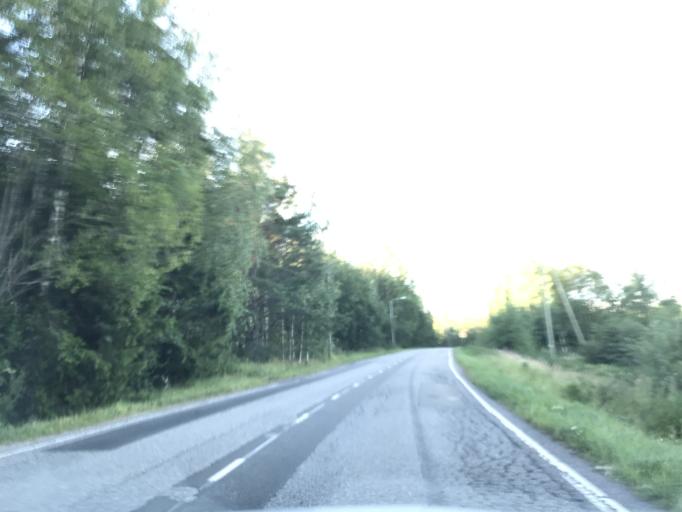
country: FI
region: Uusimaa
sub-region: Helsinki
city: Nurmijaervi
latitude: 60.3816
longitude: 24.6754
